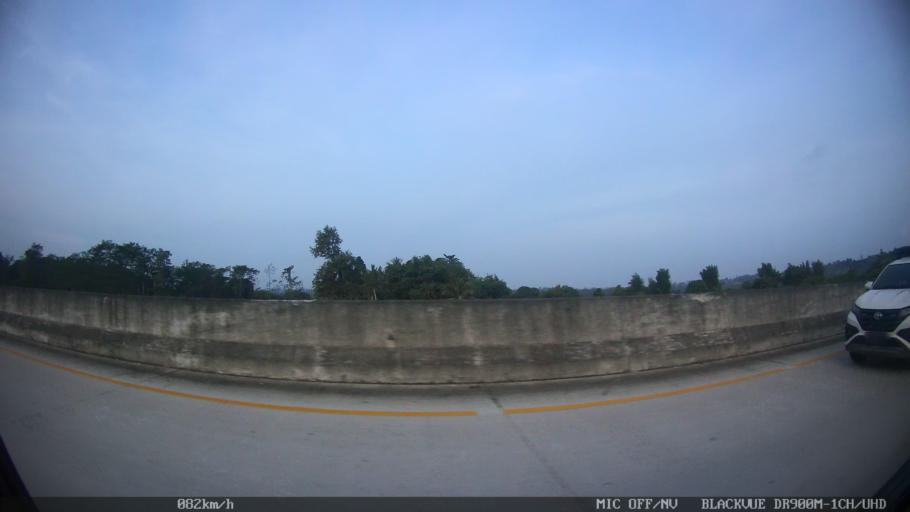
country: ID
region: Lampung
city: Penengahan
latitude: -5.7680
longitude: 105.7151
